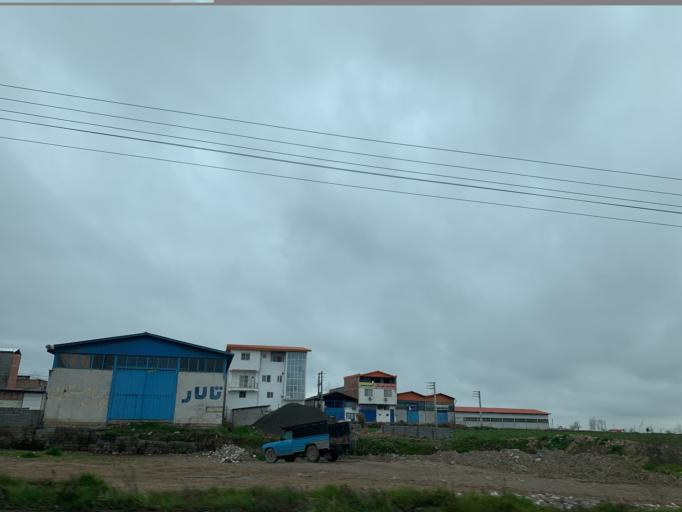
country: IR
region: Mazandaran
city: Amol
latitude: 36.4165
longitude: 52.3488
